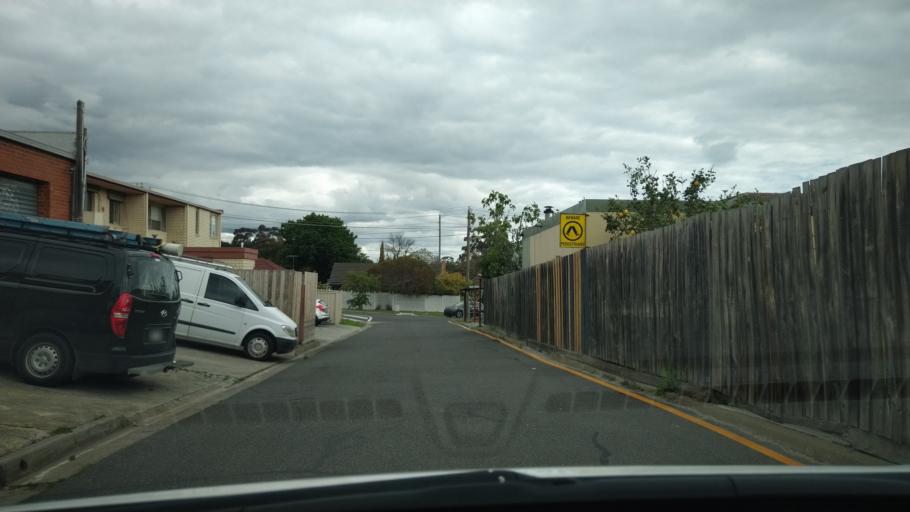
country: AU
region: Victoria
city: Highett
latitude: -37.9580
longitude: 145.0658
